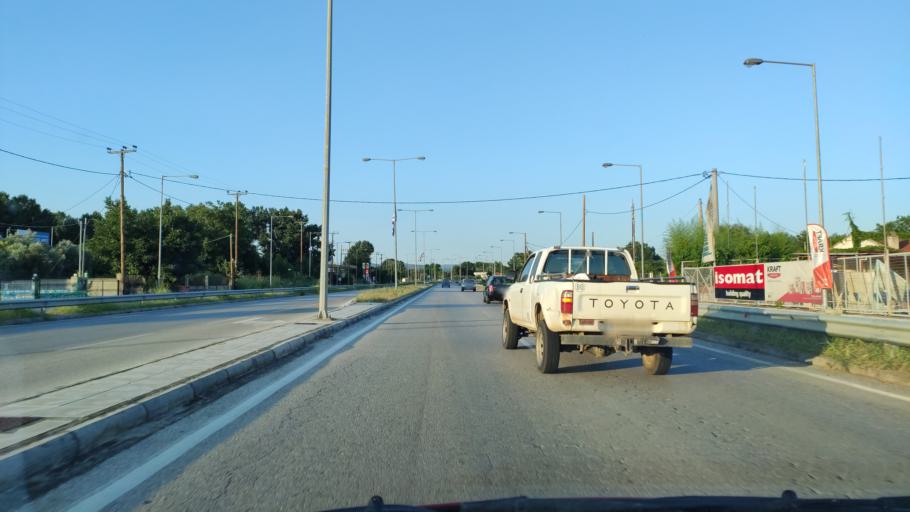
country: GR
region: East Macedonia and Thrace
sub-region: Nomos Rodopis
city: Komotini
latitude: 41.1130
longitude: 25.3764
